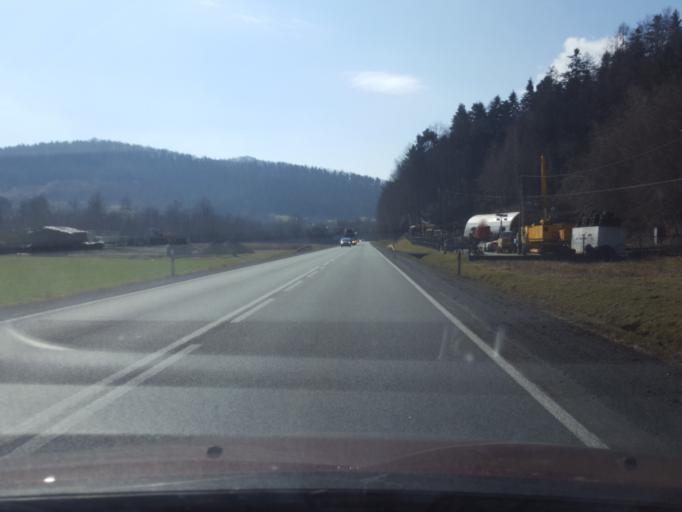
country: PL
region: Lesser Poland Voivodeship
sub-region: Powiat nowosadecki
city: Lososina Dolna
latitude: 49.7766
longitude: 20.6419
